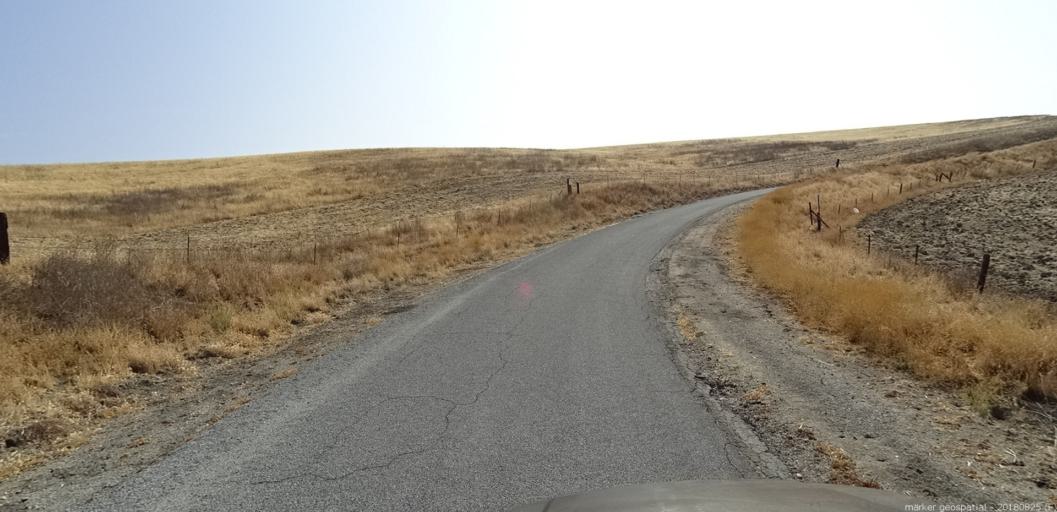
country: US
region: California
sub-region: San Luis Obispo County
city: San Miguel
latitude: 35.8124
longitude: -120.5436
